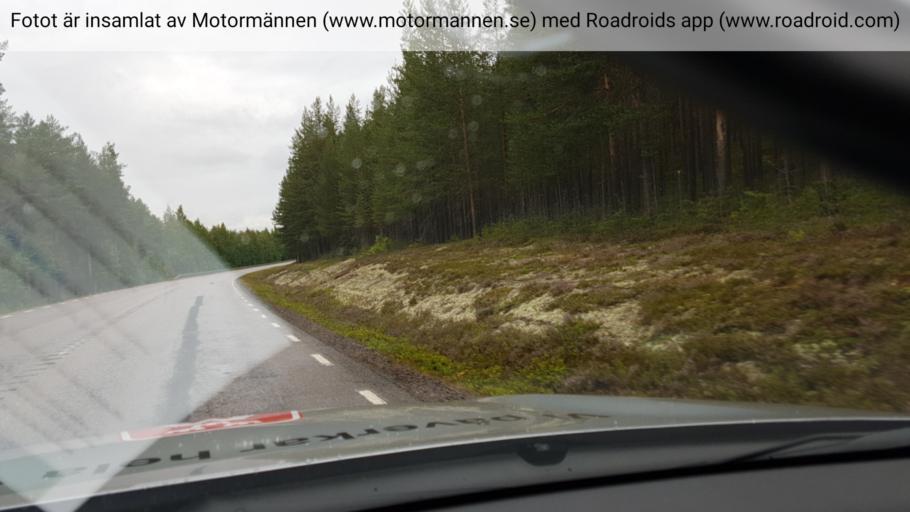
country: SE
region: Norrbotten
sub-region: Alvsbyns Kommun
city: AElvsbyn
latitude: 66.1426
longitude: 20.8801
